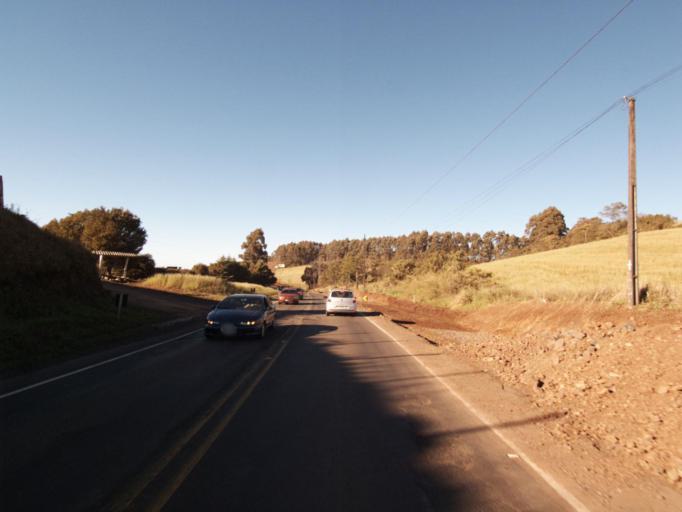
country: AR
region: Misiones
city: Bernardo de Irigoyen
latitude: -26.6172
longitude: -53.5193
